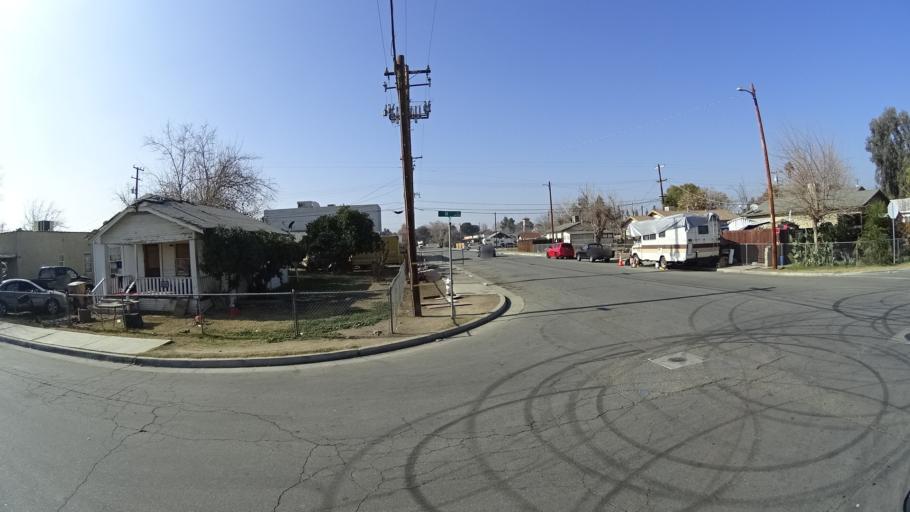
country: US
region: California
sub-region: Kern County
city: Bakersfield
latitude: 35.3923
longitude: -119.0153
